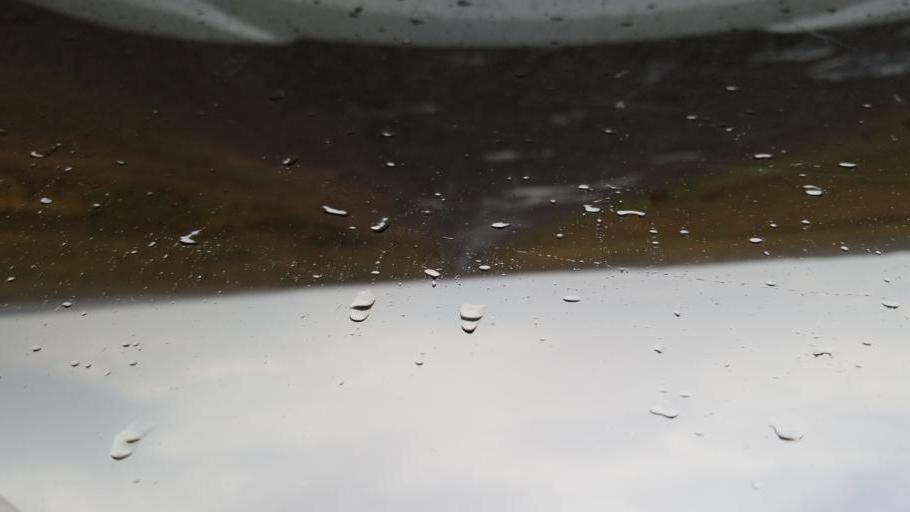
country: TM
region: Mary
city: Serhetabat
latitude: 35.8823
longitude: 62.6216
